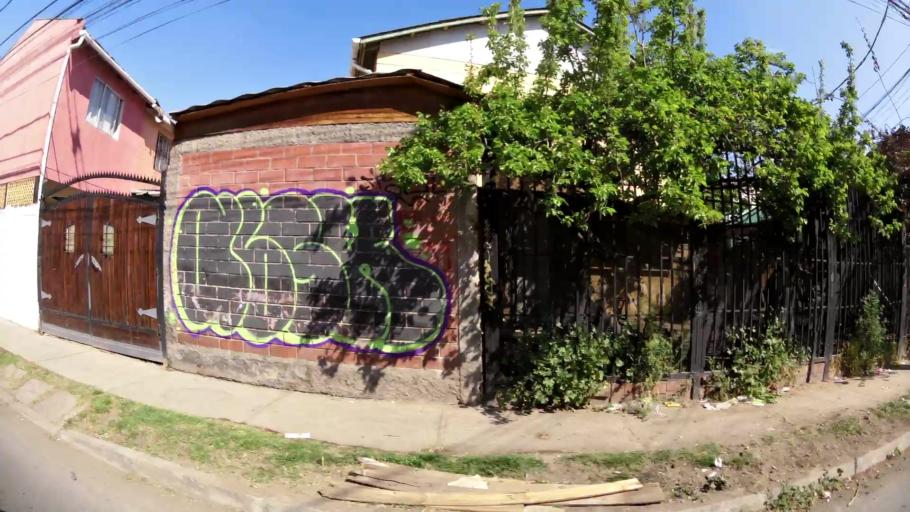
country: CL
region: Santiago Metropolitan
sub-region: Provincia de Santiago
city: Lo Prado
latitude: -33.3573
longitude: -70.7438
